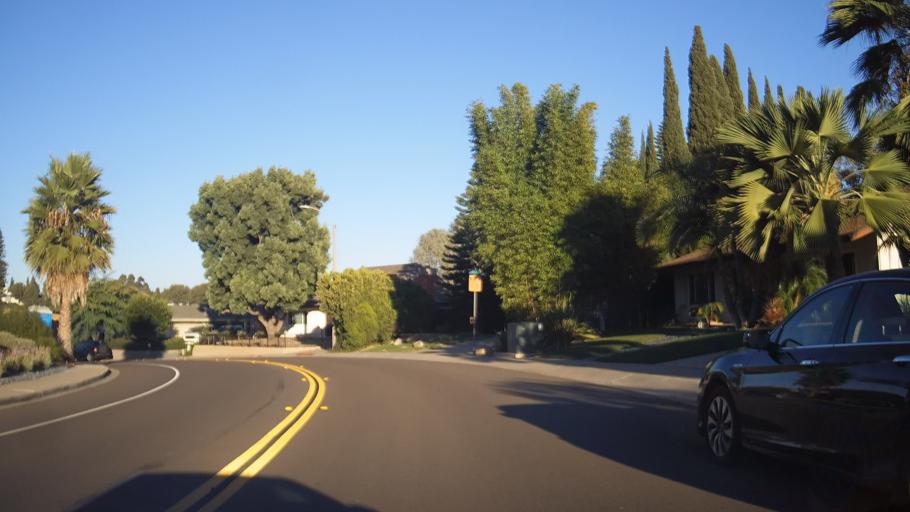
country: US
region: California
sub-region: San Diego County
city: Poway
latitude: 32.9875
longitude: -117.0870
